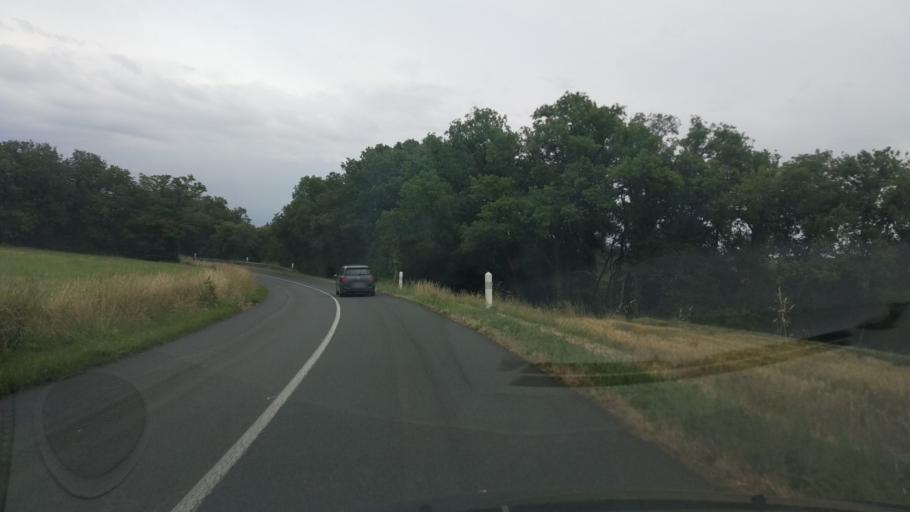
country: FR
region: Poitou-Charentes
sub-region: Departement de la Vienne
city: Biard
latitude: 46.5760
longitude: 0.2964
